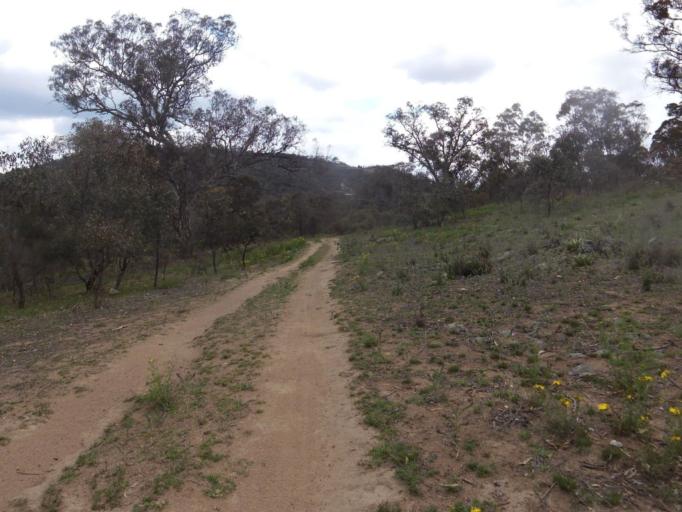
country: AU
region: Australian Capital Territory
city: Forrest
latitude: -35.3539
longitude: 149.1164
